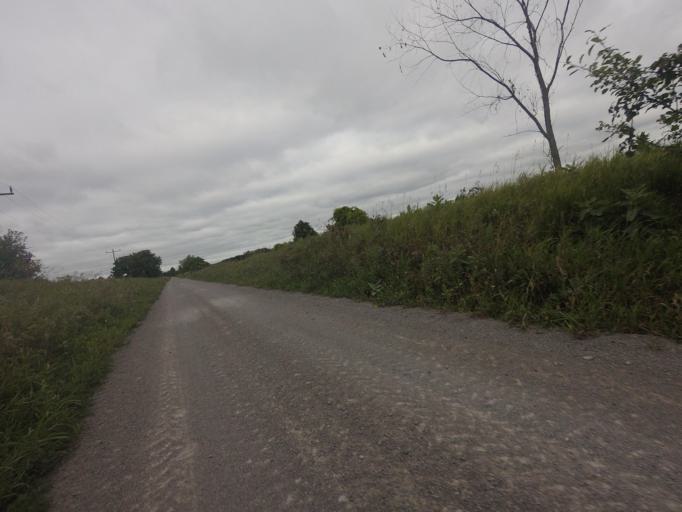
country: CA
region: Ontario
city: Omemee
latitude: 44.4570
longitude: -78.7609
